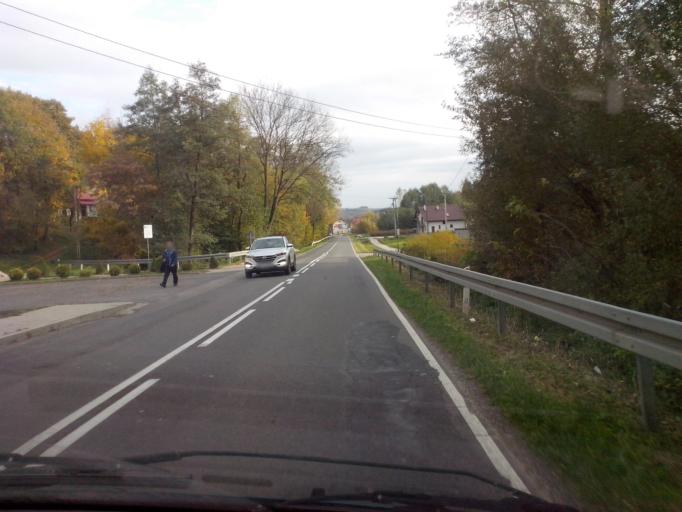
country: PL
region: Subcarpathian Voivodeship
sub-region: Powiat ropczycko-sedziszowski
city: Wielopole Skrzynskie
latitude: 49.9065
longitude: 21.6258
